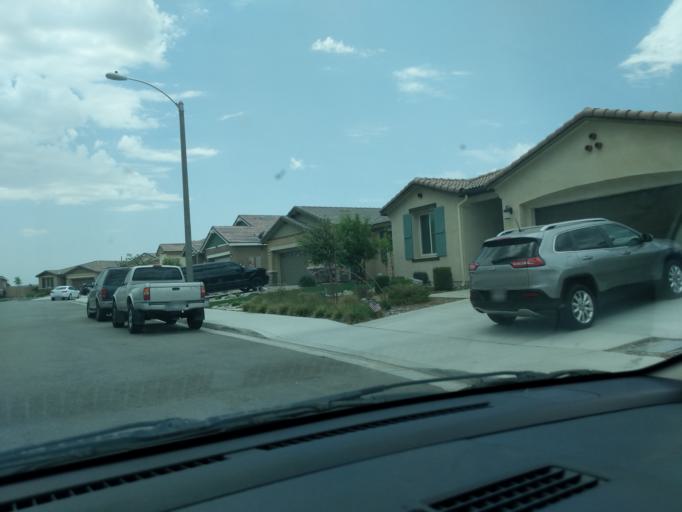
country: US
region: California
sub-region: San Bernardino County
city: Muscoy
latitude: 34.1853
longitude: -117.4237
